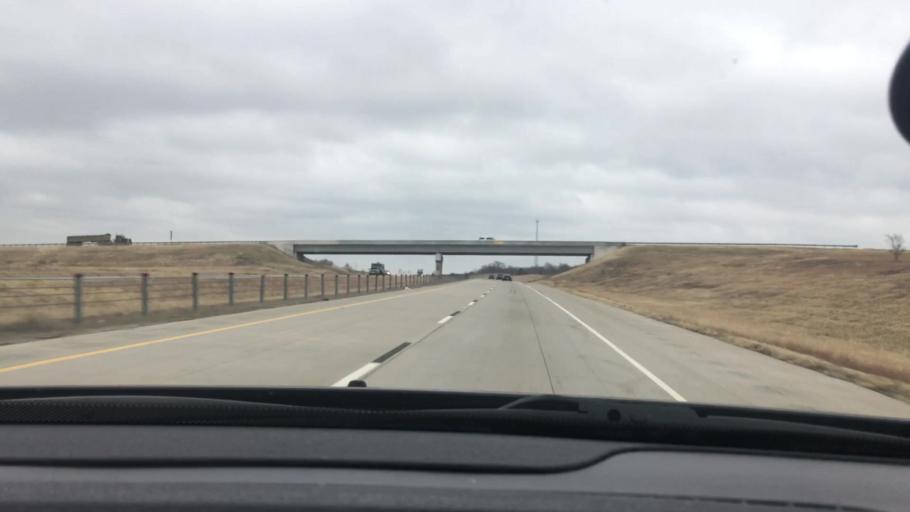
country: US
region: Oklahoma
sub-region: Bryan County
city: Durant
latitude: 34.1306
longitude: -96.2756
